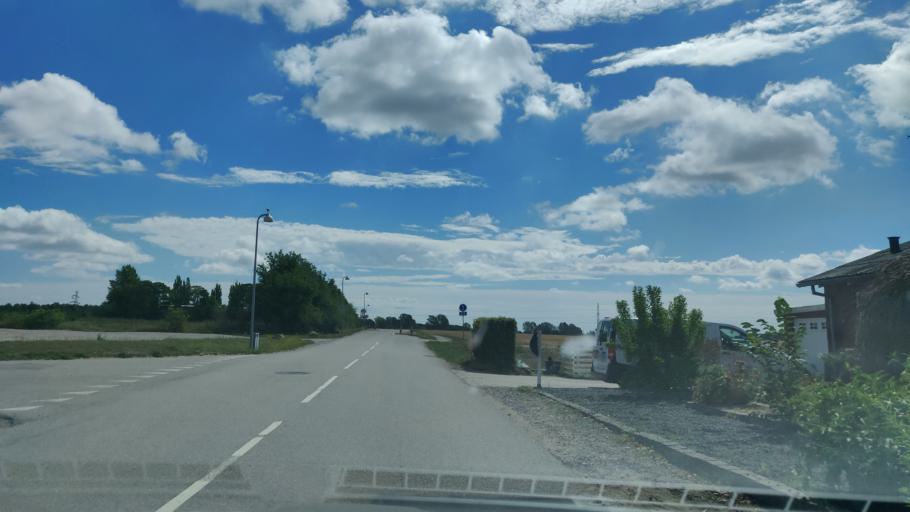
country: DK
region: Capital Region
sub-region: Hoje-Taastrup Kommune
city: Flong
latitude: 55.6633
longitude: 12.1665
